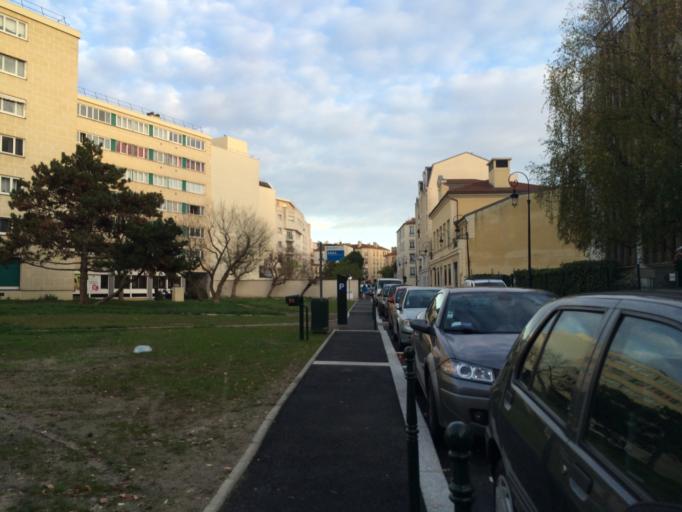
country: FR
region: Ile-de-France
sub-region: Departement des Hauts-de-Seine
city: Puteaux
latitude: 48.8796
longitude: 2.2379
